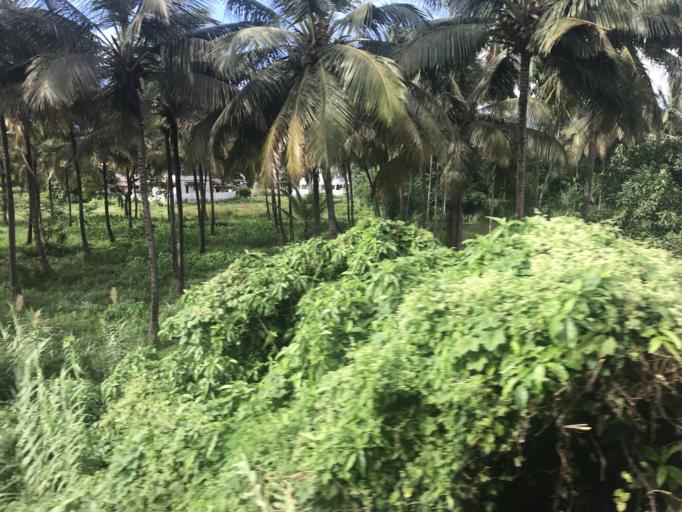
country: IN
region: Kerala
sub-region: Palakkad district
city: Palakkad
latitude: 10.8138
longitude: 76.6656
